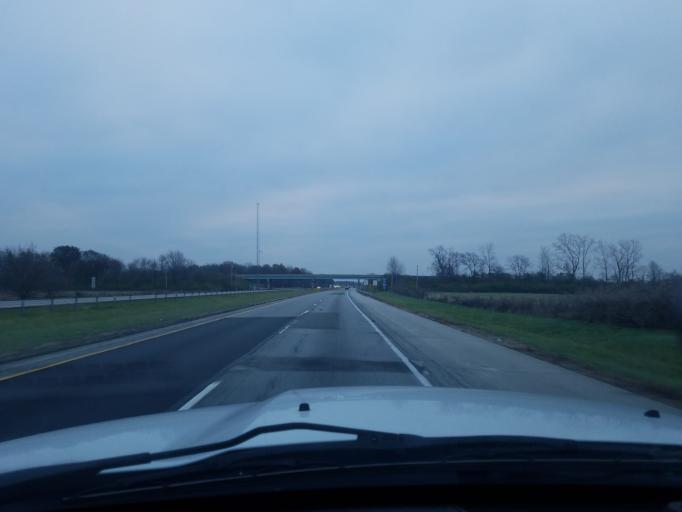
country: US
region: Indiana
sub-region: Madison County
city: Anderson
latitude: 40.0549
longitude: -85.6365
